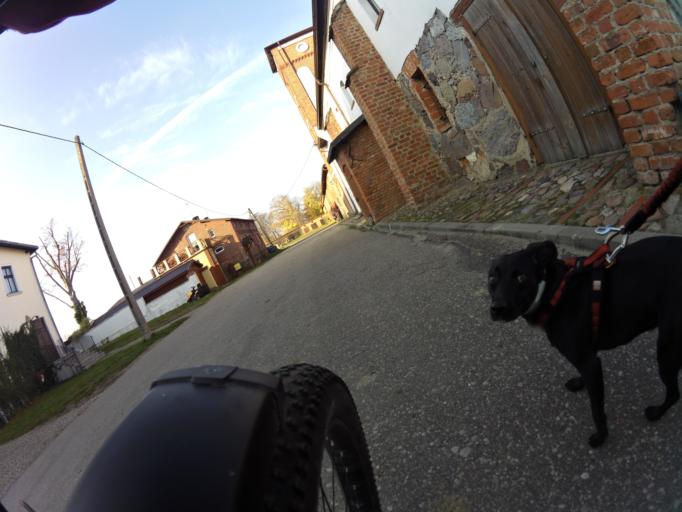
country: PL
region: Pomeranian Voivodeship
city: Strzelno
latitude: 54.7643
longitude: 18.2449
